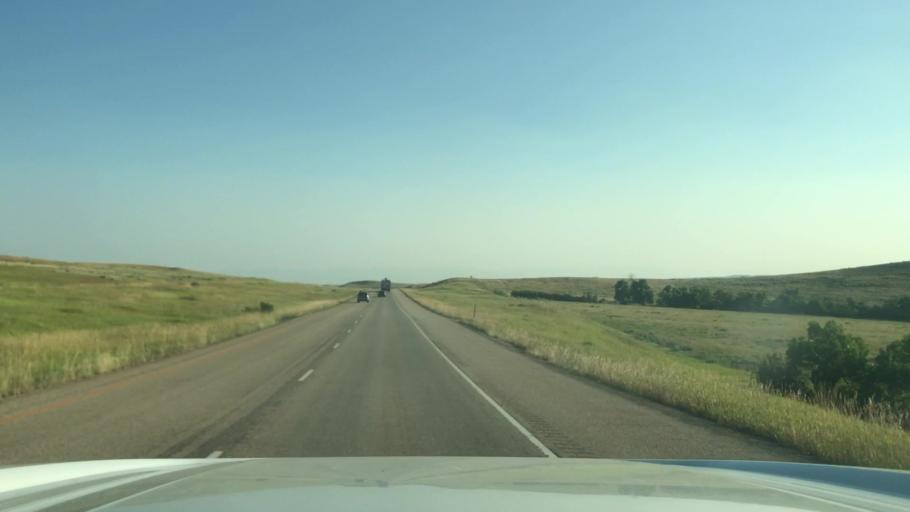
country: US
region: Montana
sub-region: Big Horn County
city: Crow Agency
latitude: 45.2584
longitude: -107.3514
